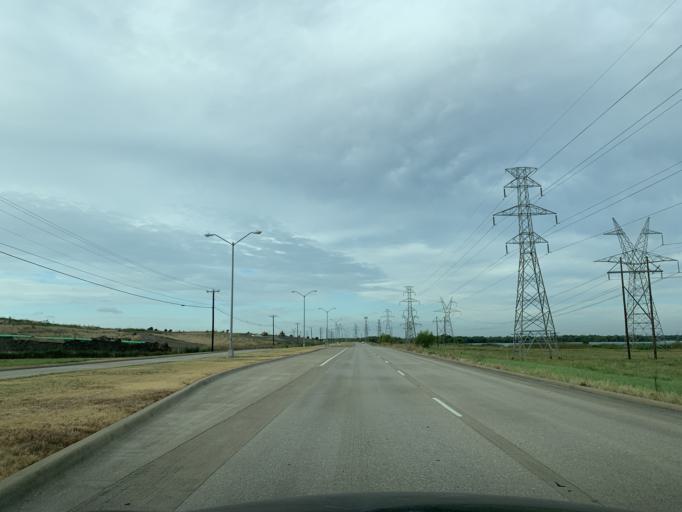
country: US
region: Texas
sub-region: Dallas County
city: Grand Prairie
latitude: 32.7021
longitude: -96.9577
